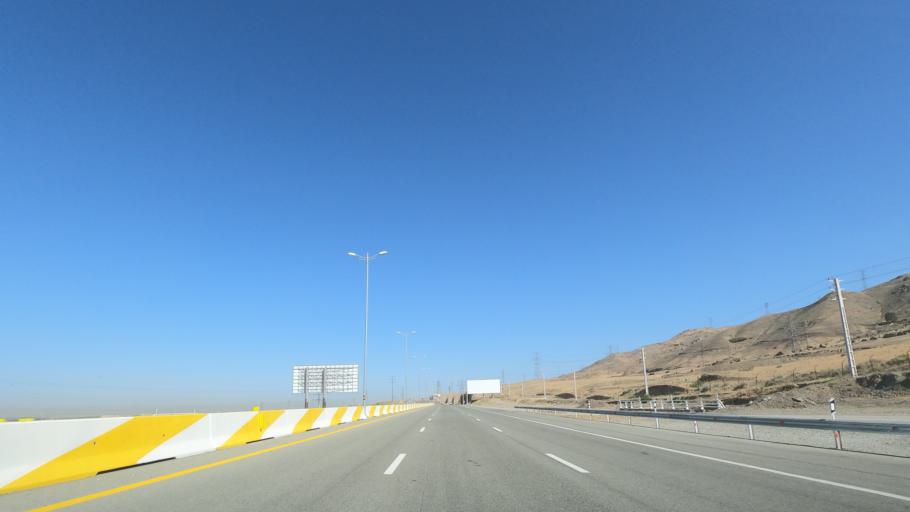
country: IR
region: Tehran
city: Shahr-e Qods
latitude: 35.7691
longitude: 51.0627
